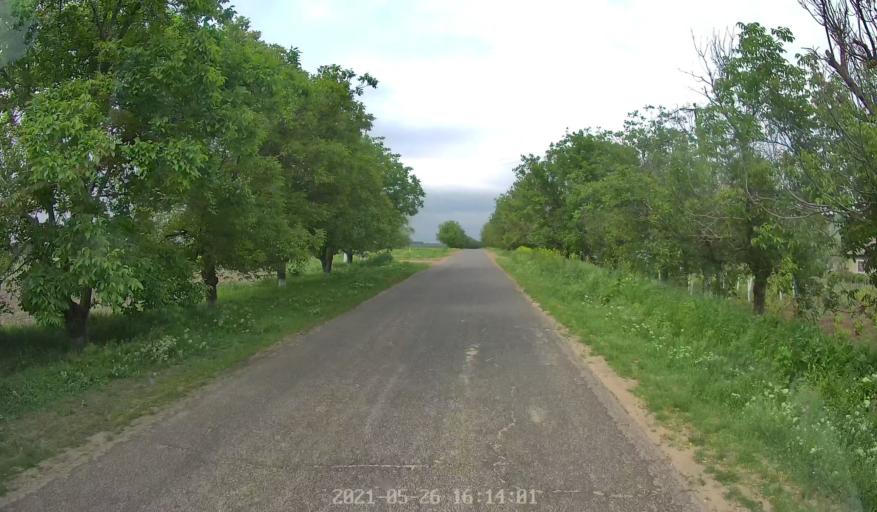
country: MD
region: Hincesti
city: Dancu
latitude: 46.7062
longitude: 28.3400
